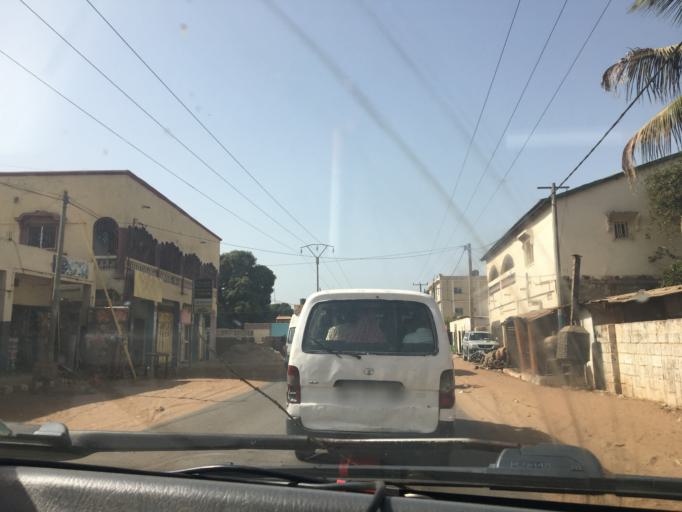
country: GM
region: Western
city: Abuko
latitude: 13.3999
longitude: -16.6733
